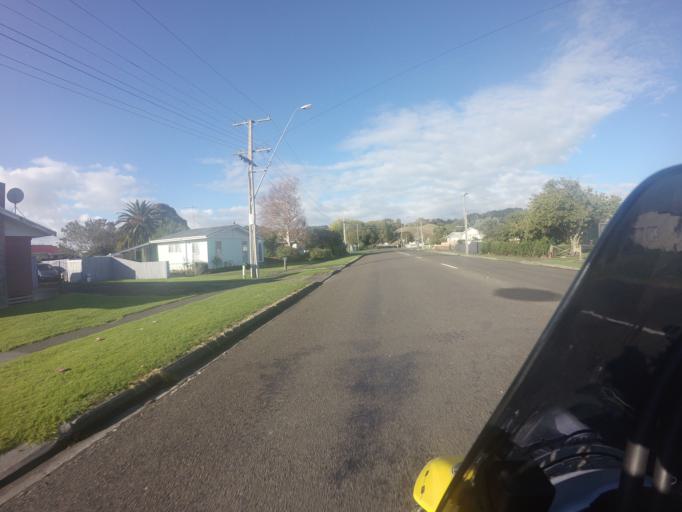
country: NZ
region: Gisborne
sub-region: Gisborne District
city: Gisborne
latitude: -38.6754
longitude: 178.0490
